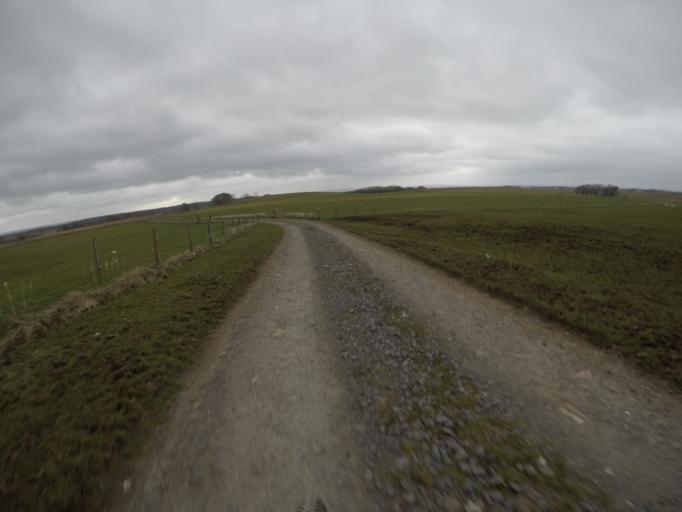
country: GB
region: Scotland
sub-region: East Ayrshire
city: Galston
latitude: 55.6720
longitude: -4.3732
